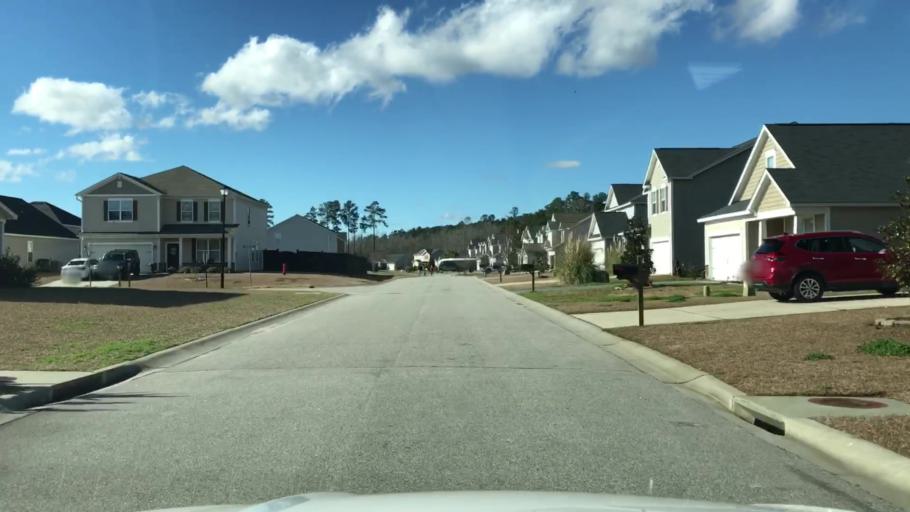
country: US
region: South Carolina
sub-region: Dorchester County
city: Summerville
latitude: 33.0903
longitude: -80.1939
